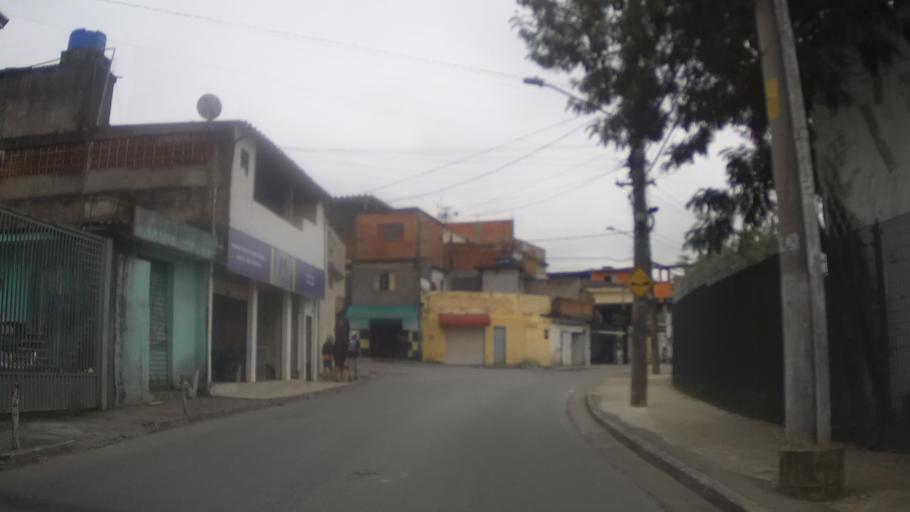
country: BR
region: Sao Paulo
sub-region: Guarulhos
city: Guarulhos
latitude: -23.4307
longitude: -46.5162
